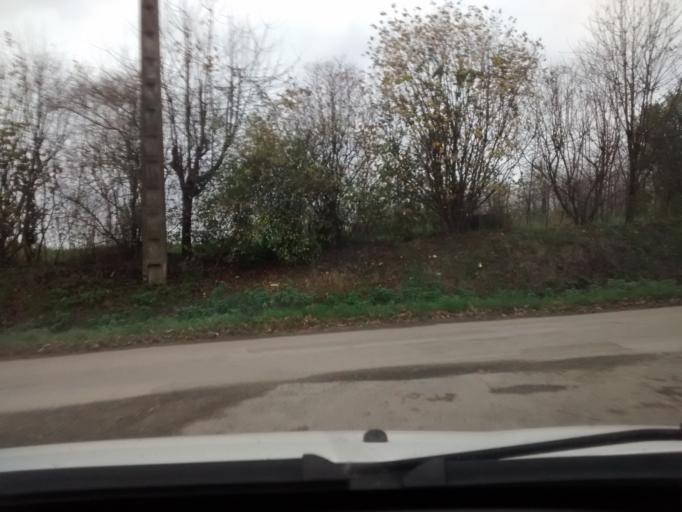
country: FR
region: Brittany
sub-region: Departement d'Ille-et-Vilaine
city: Brece
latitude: 48.1428
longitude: -1.4949
